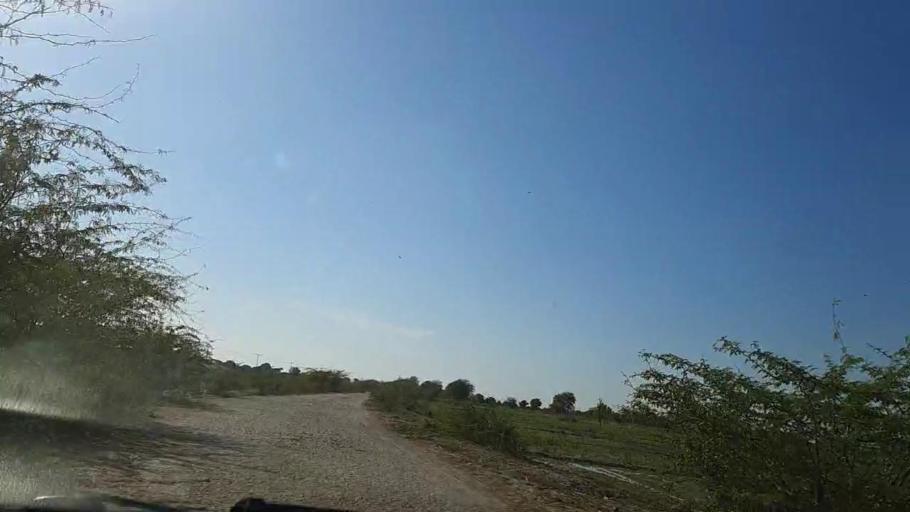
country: PK
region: Sindh
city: Dhoro Naro
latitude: 25.5037
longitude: 69.5531
